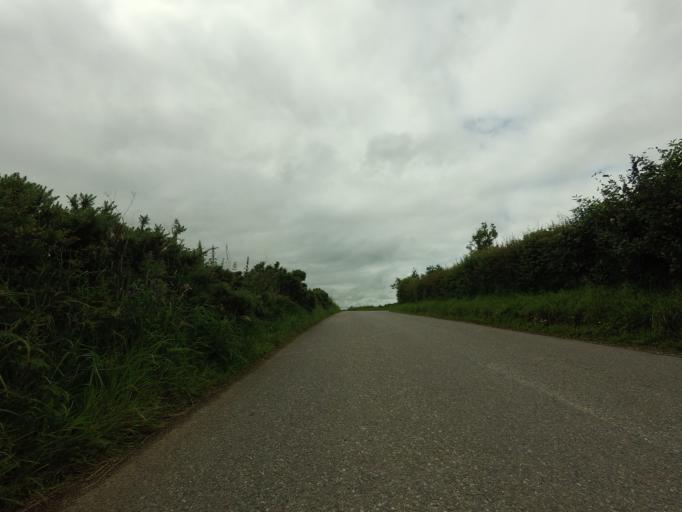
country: GB
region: Scotland
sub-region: Aberdeenshire
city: Mintlaw
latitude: 57.5260
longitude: -2.1449
